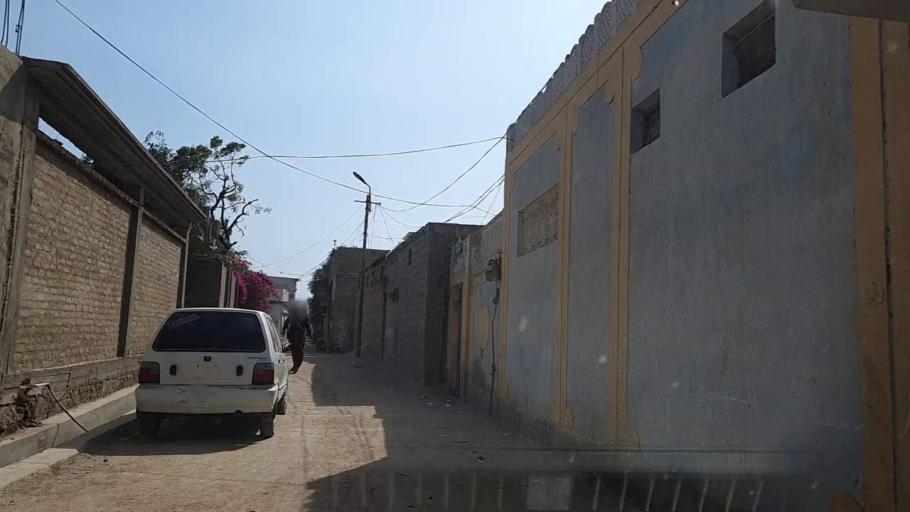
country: PK
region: Sindh
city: Daro Mehar
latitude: 24.7964
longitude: 68.1796
